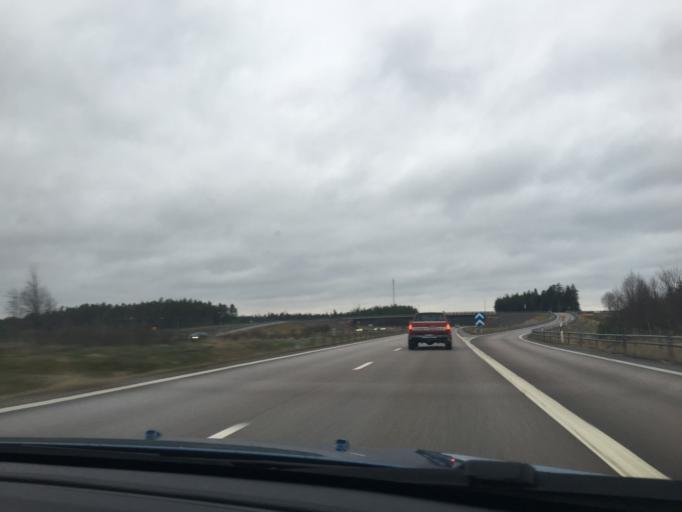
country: SE
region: Uppsala
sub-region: Tierps Kommun
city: Tierp
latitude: 60.4366
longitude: 17.4234
